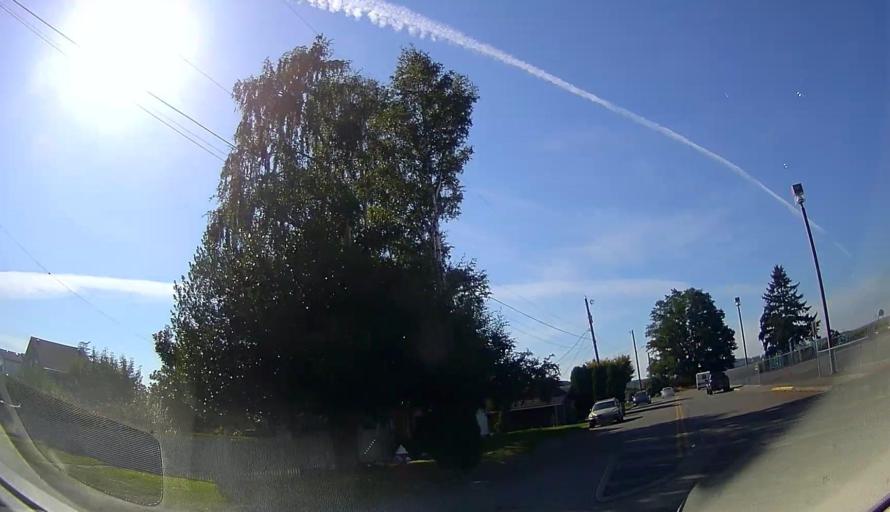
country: US
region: Washington
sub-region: Snohomish County
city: Stanwood
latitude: 48.2446
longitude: -122.3731
